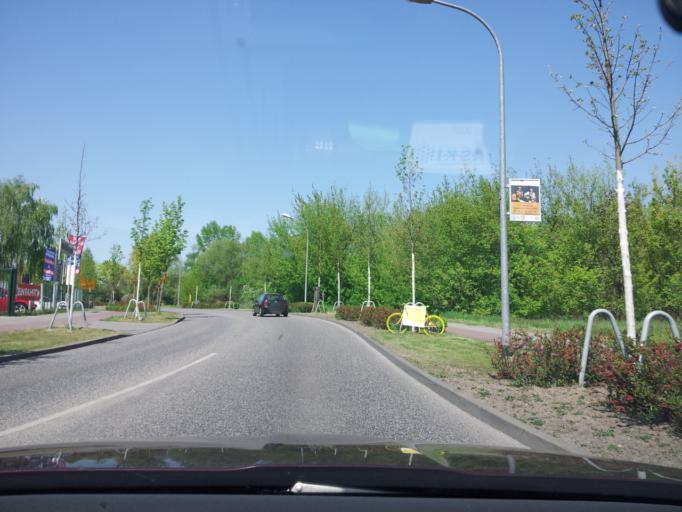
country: DE
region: Brandenburg
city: Teltow
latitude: 52.4022
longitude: 13.2718
